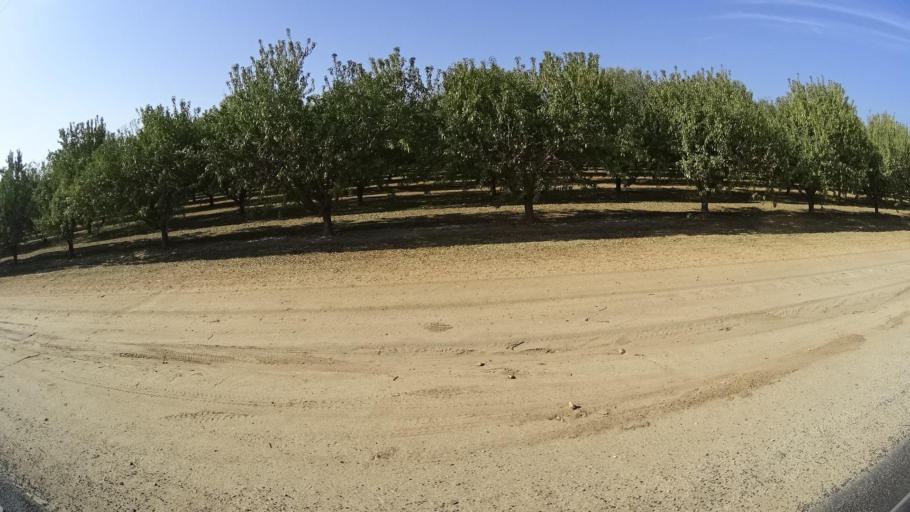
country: US
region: California
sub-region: Kern County
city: Shafter
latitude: 35.5077
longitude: -119.1522
